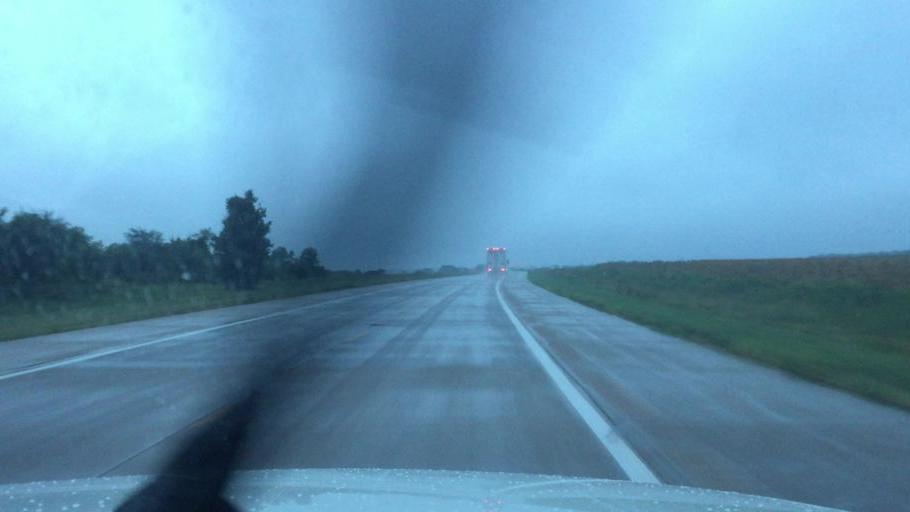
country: US
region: Kansas
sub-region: Neosho County
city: Chanute
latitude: 37.5359
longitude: -95.4709
